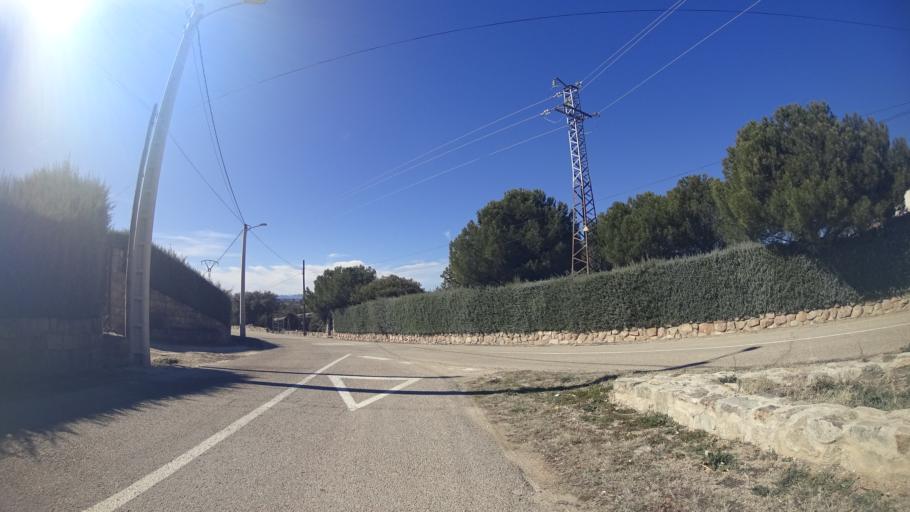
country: ES
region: Madrid
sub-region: Provincia de Madrid
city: Colmenarejo
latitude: 40.5498
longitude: -3.9930
